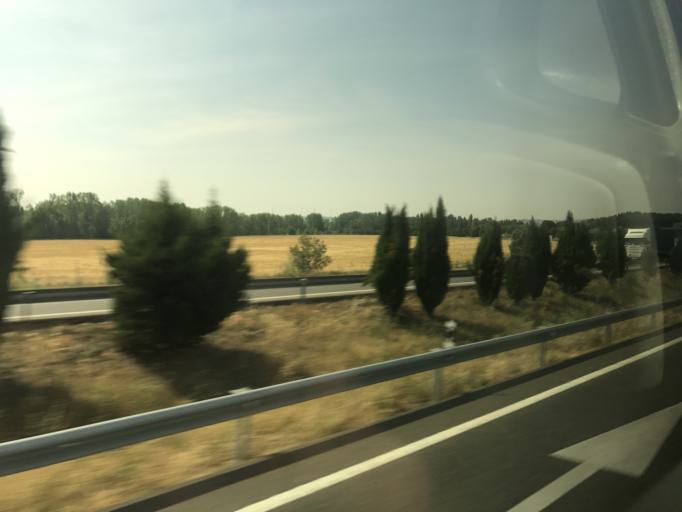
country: ES
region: Castille and Leon
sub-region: Provincia de Palencia
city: Quintana del Puente
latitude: 42.0934
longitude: -4.2079
